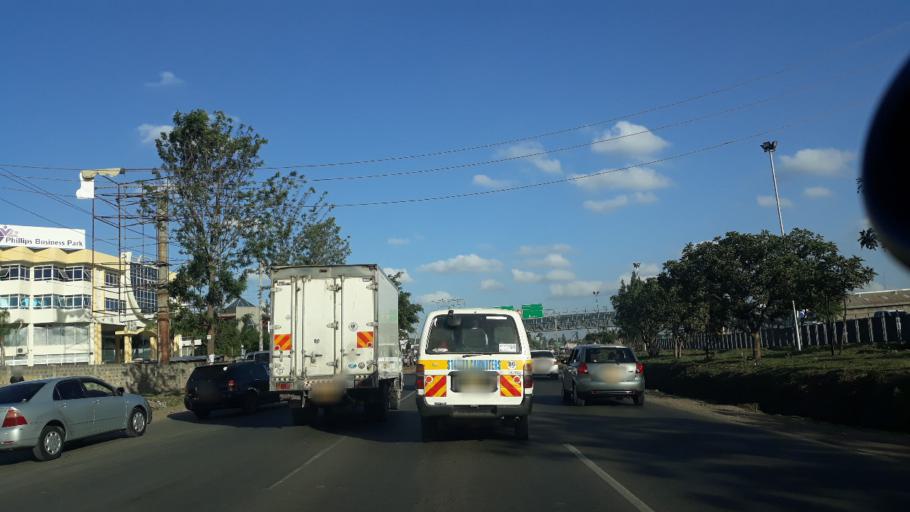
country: KE
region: Nairobi Area
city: Pumwani
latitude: -1.3285
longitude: 36.8826
